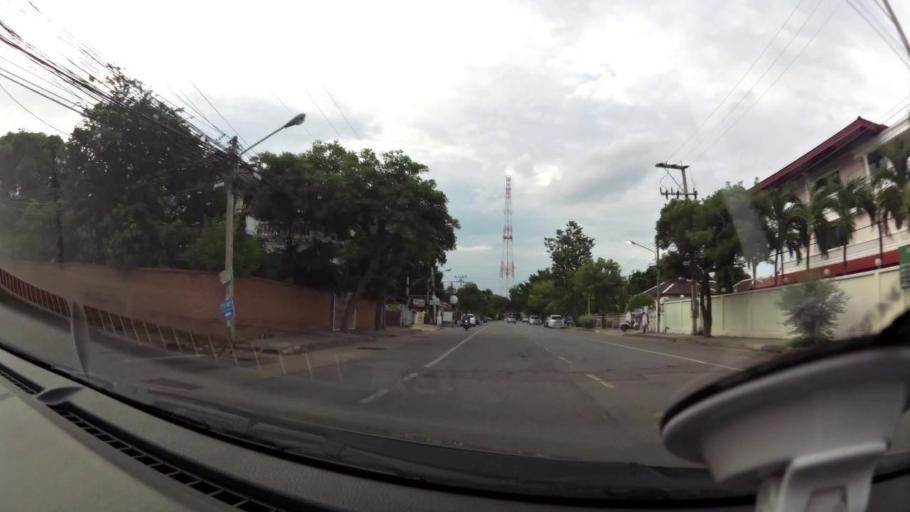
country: TH
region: Prachuap Khiri Khan
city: Hua Hin
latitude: 12.5839
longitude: 99.9554
